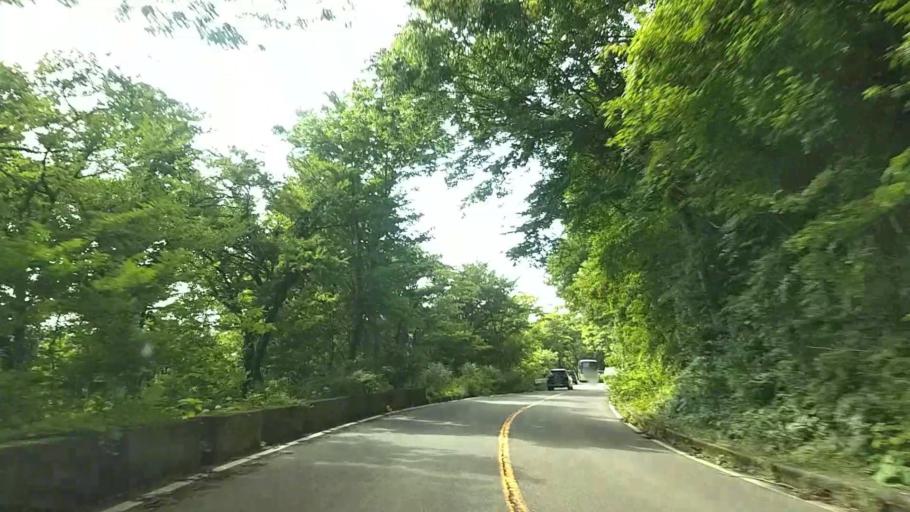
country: JP
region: Kanagawa
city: Hakone
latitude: 35.2278
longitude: 139.0005
